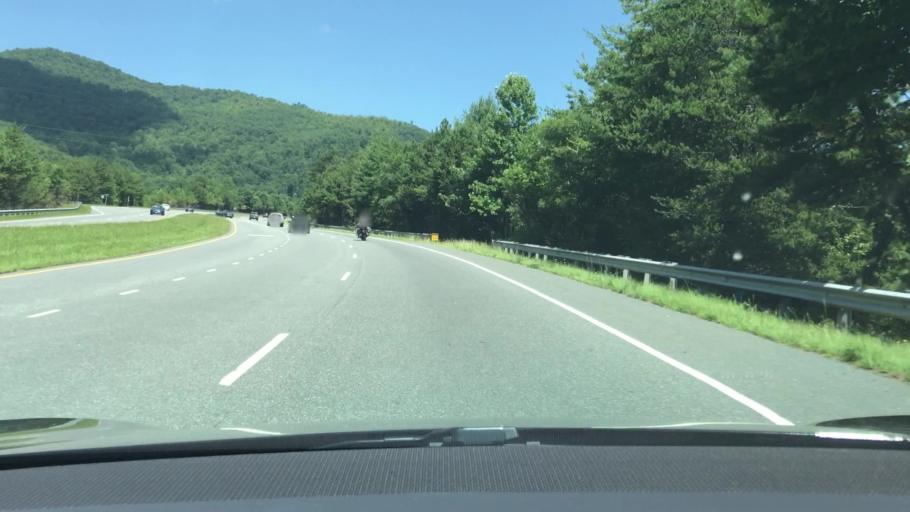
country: US
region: North Carolina
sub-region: Jackson County
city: Sylva
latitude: 35.3403
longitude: -83.2530
